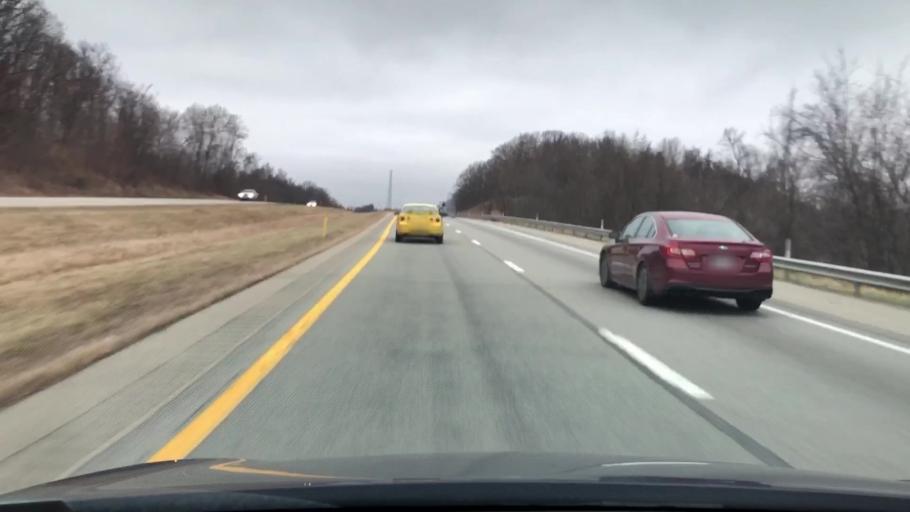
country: US
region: Pennsylvania
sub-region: Greene County
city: Morrisville
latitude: 39.8412
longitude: -80.1130
